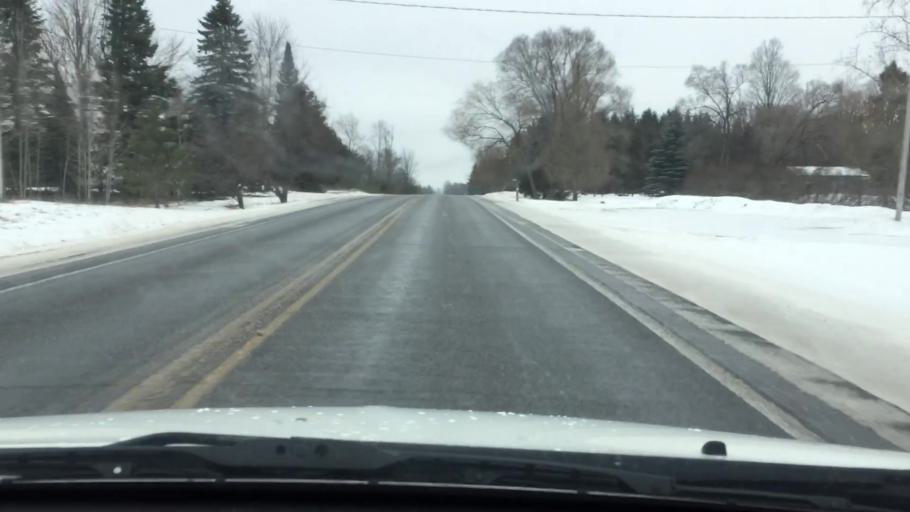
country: US
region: Michigan
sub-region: Wexford County
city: Cadillac
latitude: 44.0927
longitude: -85.4442
